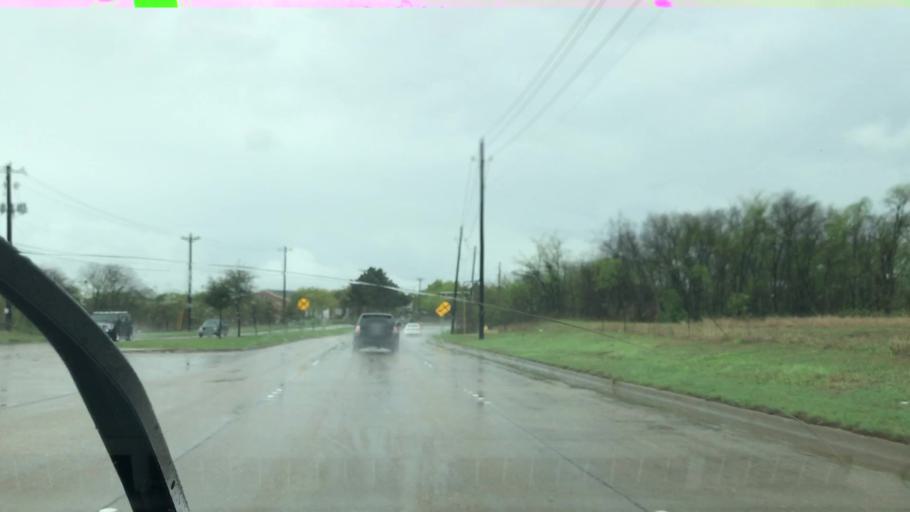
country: US
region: Texas
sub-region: Denton County
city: The Colony
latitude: 33.0429
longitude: -96.8813
